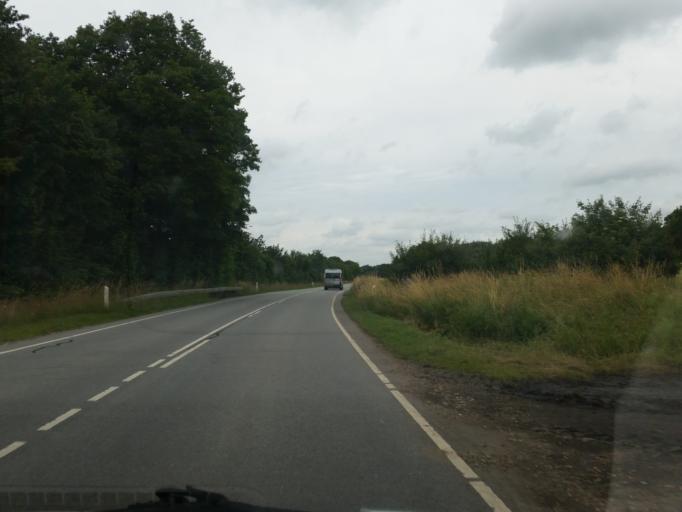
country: DK
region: South Denmark
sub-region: Vejen Kommune
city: Brorup
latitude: 55.4154
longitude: 8.9455
